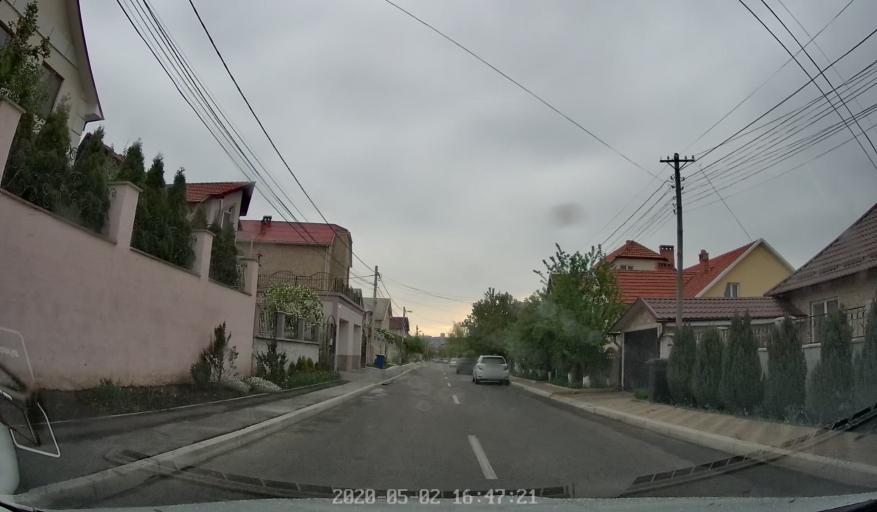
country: MD
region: Chisinau
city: Chisinau
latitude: 46.9620
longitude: 28.8325
